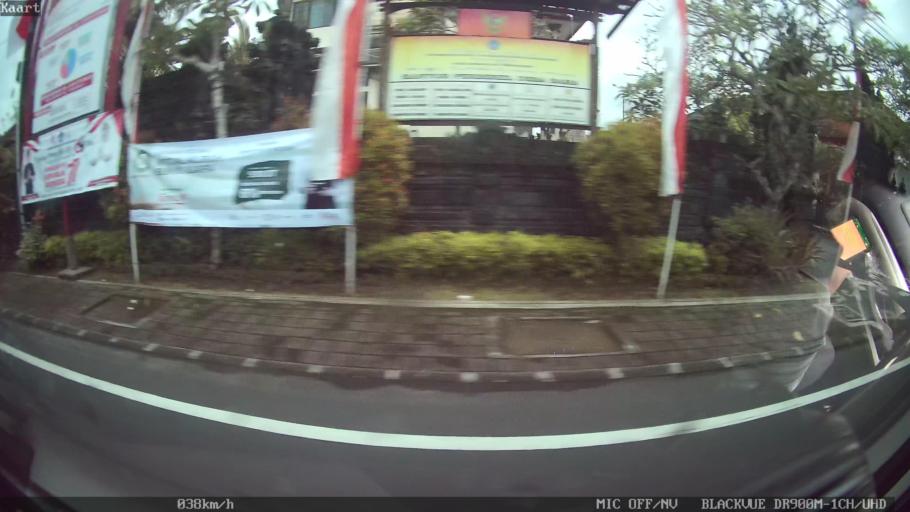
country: ID
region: Bali
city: Banjar Sayanbaleran
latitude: -8.5187
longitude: 115.1871
